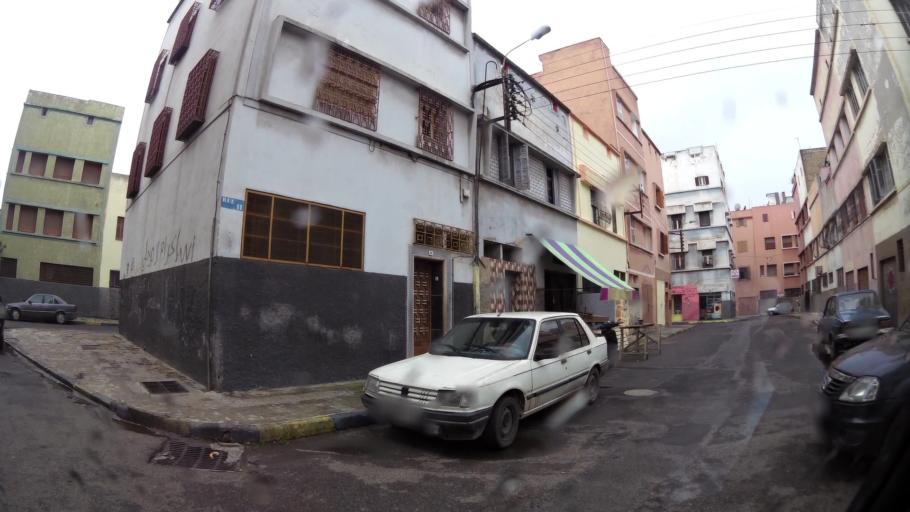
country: MA
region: Grand Casablanca
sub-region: Casablanca
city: Casablanca
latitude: 33.5702
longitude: -7.5933
